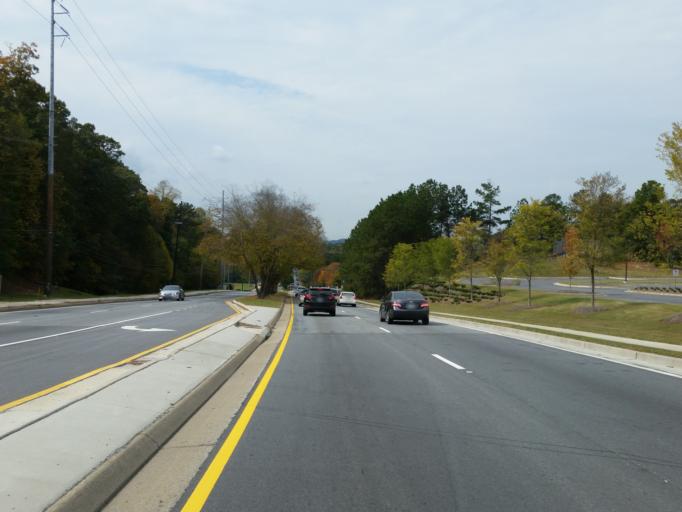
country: US
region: Georgia
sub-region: Fulton County
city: Sandy Springs
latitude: 33.9791
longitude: -84.4452
